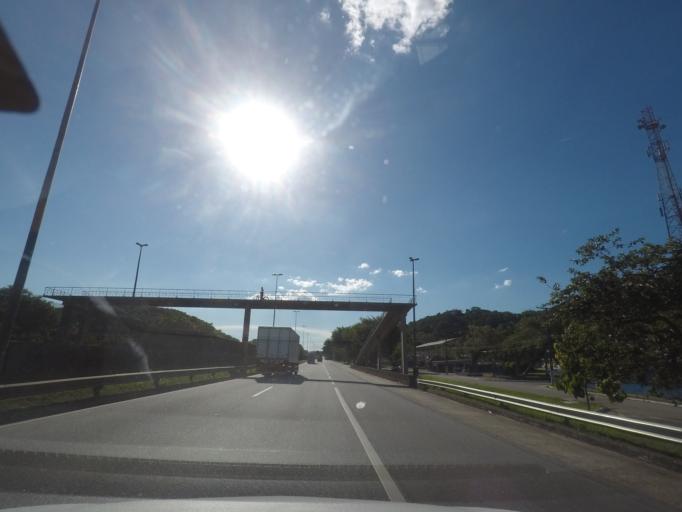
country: BR
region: Rio de Janeiro
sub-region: Petropolis
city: Petropolis
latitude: -22.6536
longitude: -43.1512
